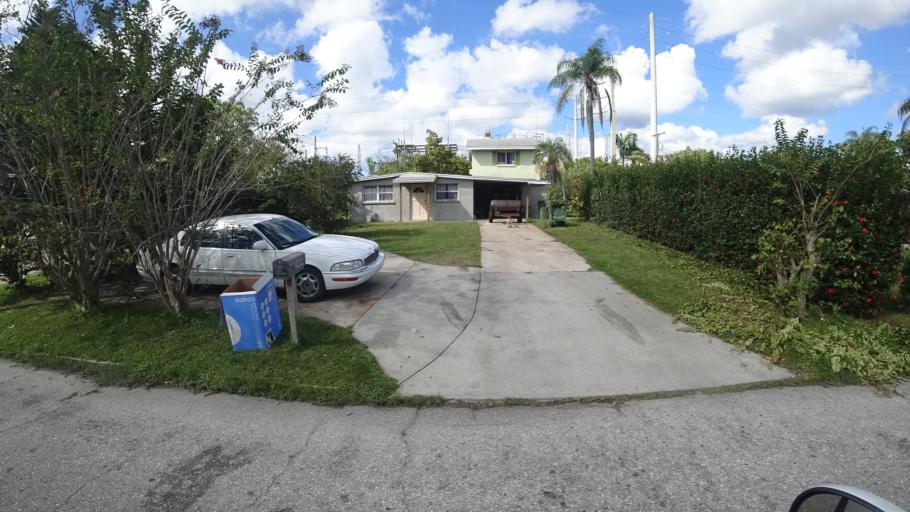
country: US
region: Florida
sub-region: Manatee County
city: Samoset
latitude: 27.4865
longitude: -82.5485
